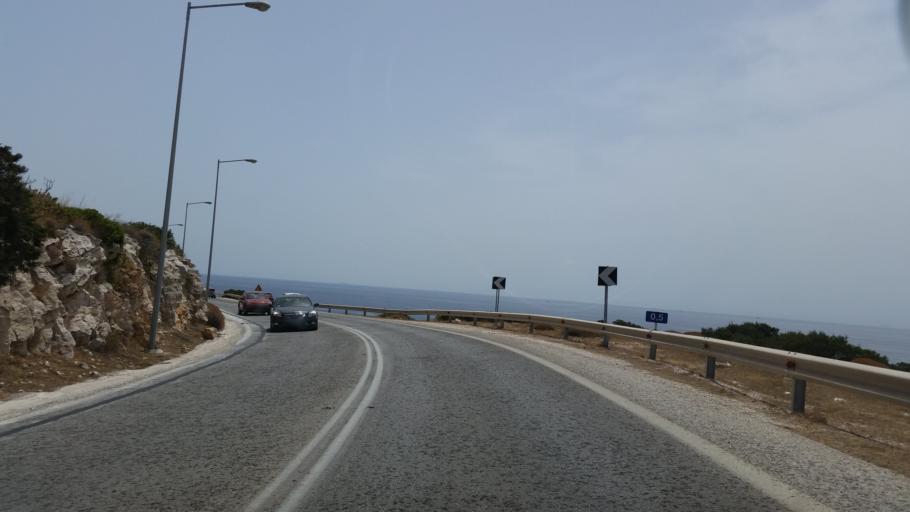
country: GR
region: Attica
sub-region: Nomarchia Anatolikis Attikis
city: Palaia Fokaia
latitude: 37.7091
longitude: 23.9368
